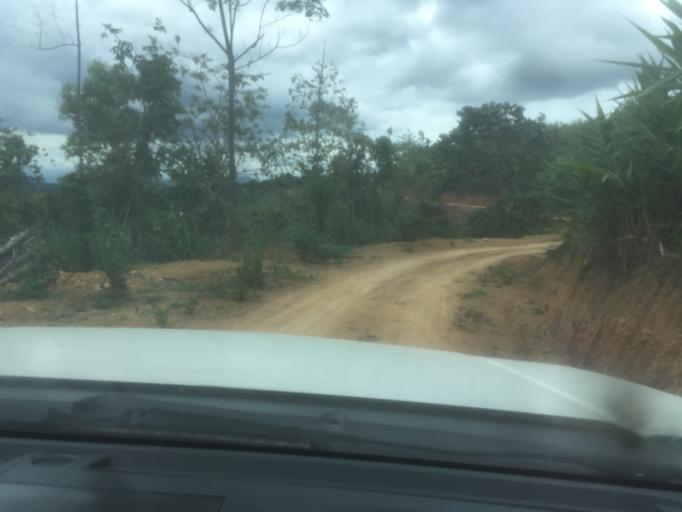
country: LA
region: Phongsali
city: Khoa
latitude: 20.9260
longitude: 102.5426
